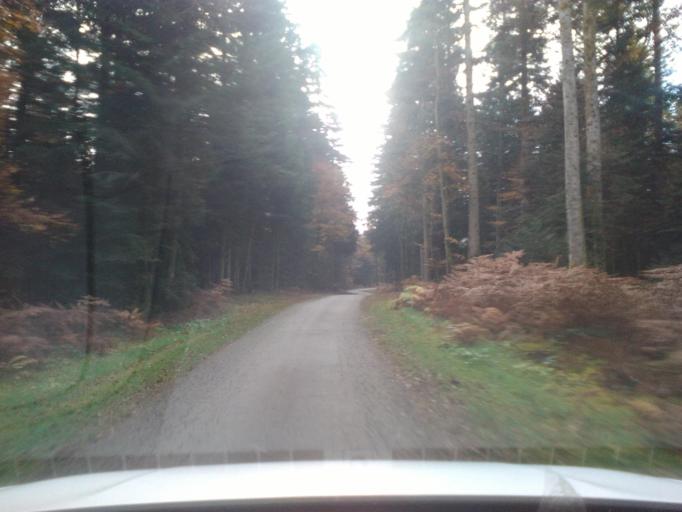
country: FR
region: Lorraine
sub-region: Departement des Vosges
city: Moyenmoutier
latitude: 48.3587
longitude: 6.9039
